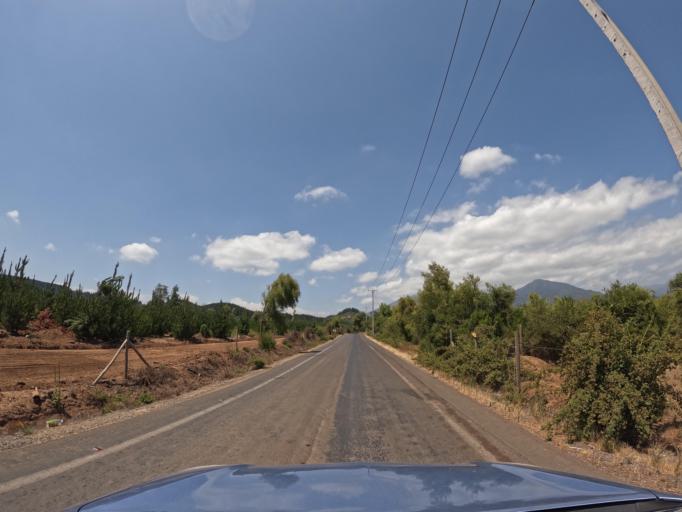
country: CL
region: Maule
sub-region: Provincia de Curico
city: Molina
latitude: -35.1790
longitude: -71.1099
